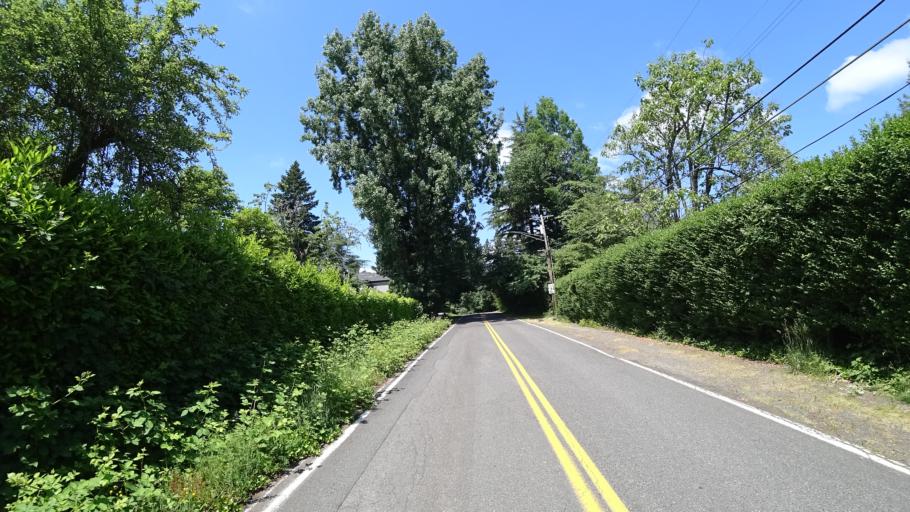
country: US
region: Oregon
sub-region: Clackamas County
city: Lake Oswego
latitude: 45.4401
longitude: -122.6935
